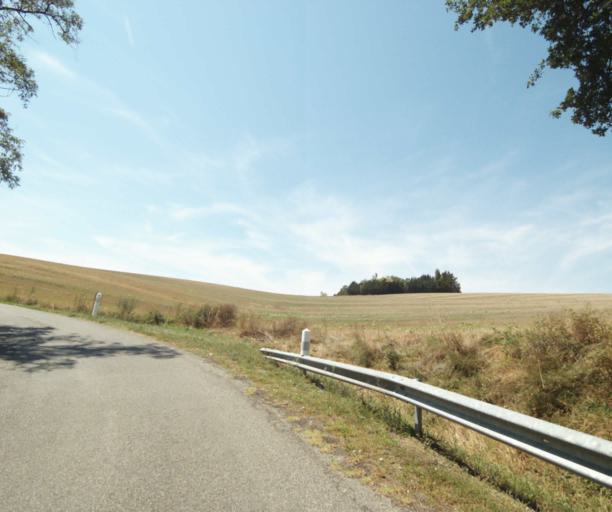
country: FR
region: Midi-Pyrenees
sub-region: Departement de l'Ariege
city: Lezat-sur-Leze
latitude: 43.2592
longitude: 1.3197
